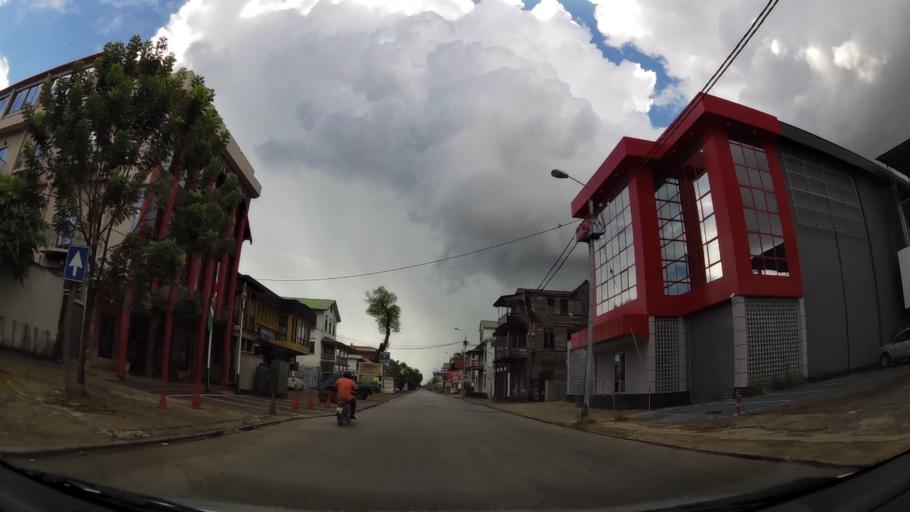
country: SR
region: Paramaribo
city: Paramaribo
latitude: 5.8290
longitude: -55.1609
